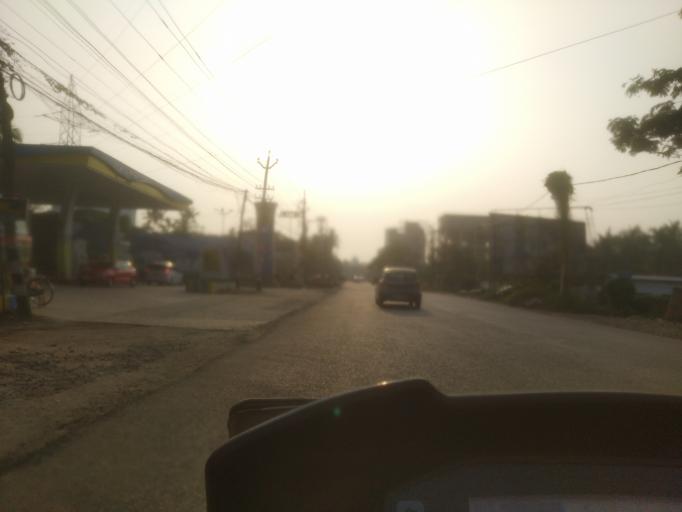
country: IN
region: Kerala
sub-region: Ernakulam
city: Cochin
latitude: 9.9378
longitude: 76.3215
